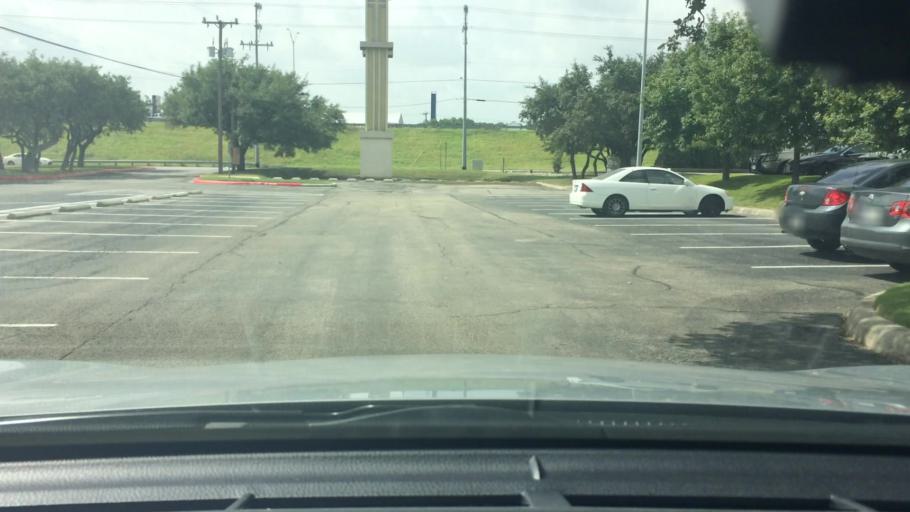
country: US
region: Texas
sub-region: Bexar County
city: Hollywood Park
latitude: 29.6100
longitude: -98.4945
